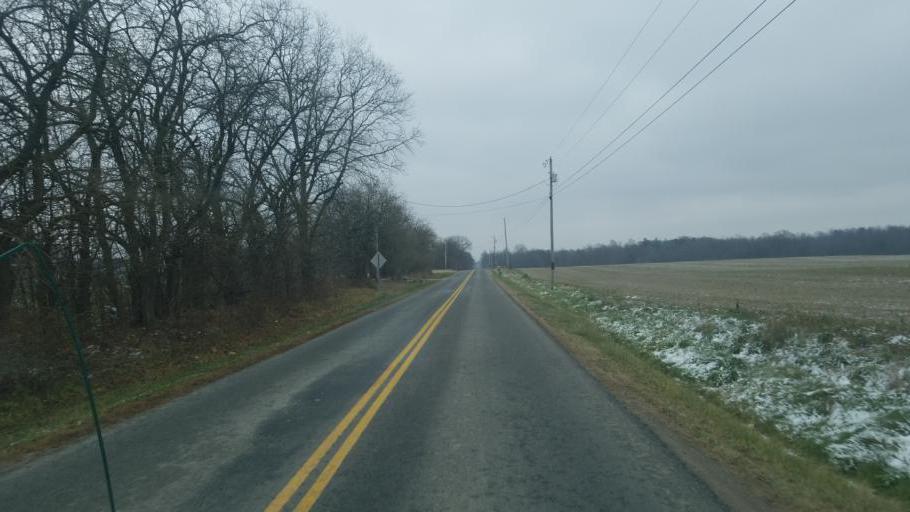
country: US
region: Ohio
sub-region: Medina County
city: Lodi
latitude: 41.1125
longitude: -82.0224
